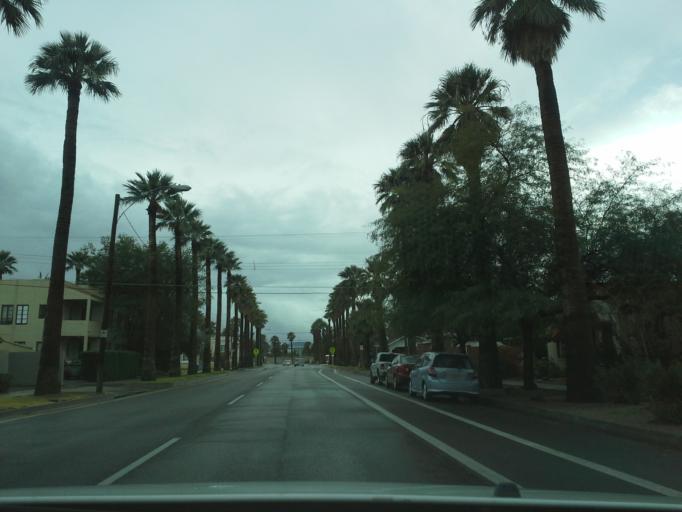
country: US
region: Arizona
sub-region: Maricopa County
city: Phoenix
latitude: 33.4647
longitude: -112.0803
